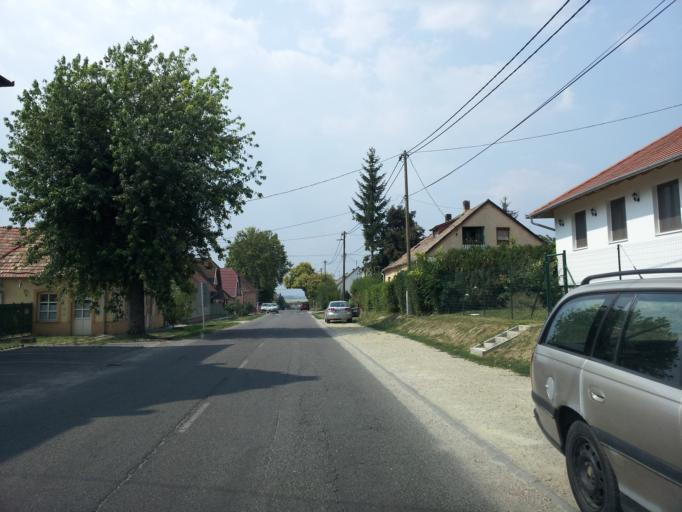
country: HU
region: Gyor-Moson-Sopron
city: Pannonhalma
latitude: 47.5512
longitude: 17.7529
